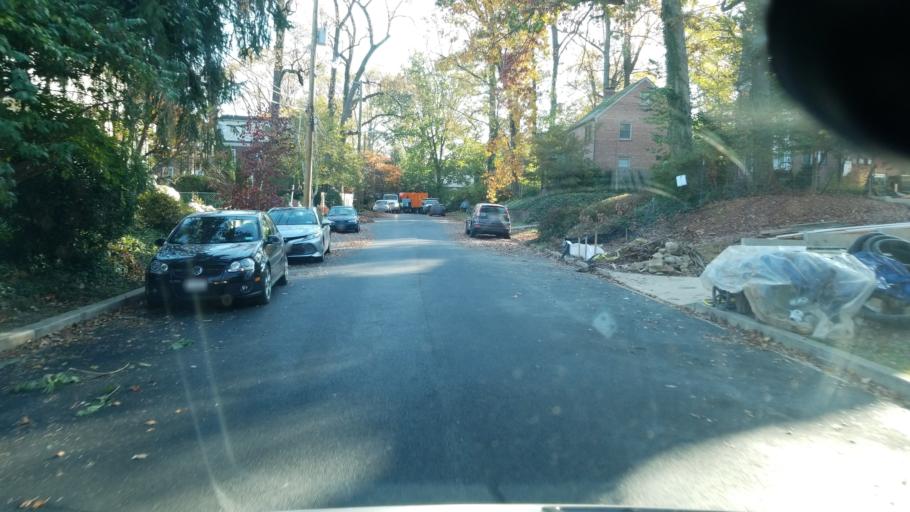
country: US
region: Maryland
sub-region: Montgomery County
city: Chevy Chase
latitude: 38.9740
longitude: -77.0677
